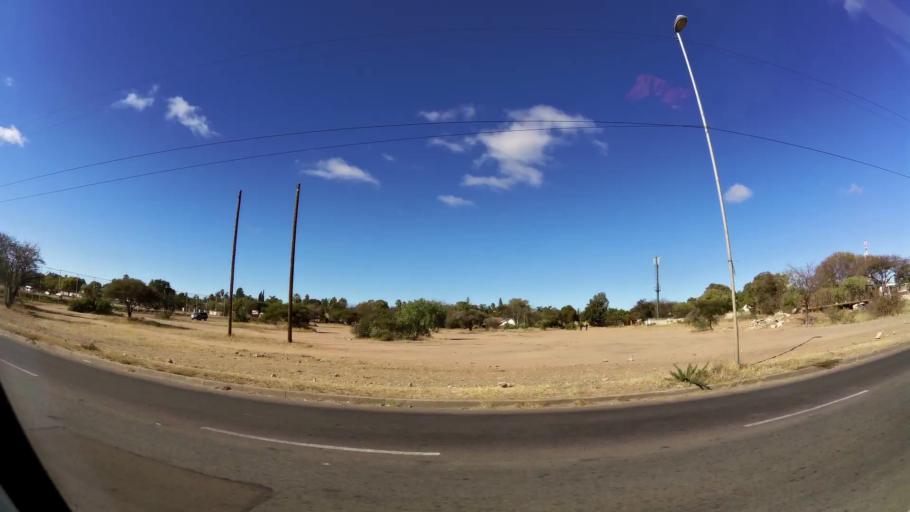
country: ZA
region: Limpopo
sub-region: Capricorn District Municipality
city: Polokwane
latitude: -23.8735
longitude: 29.4524
